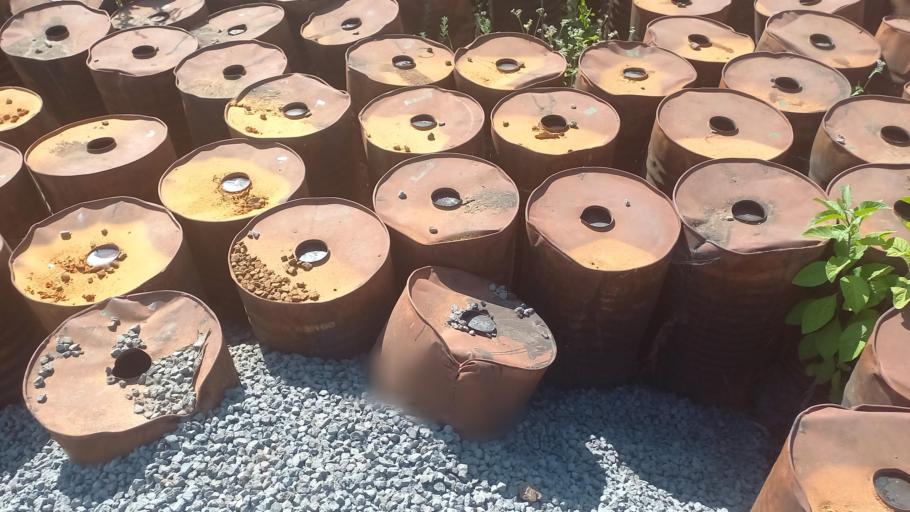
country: ET
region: Southern Nations, Nationalities, and People's Region
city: K'olito
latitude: 7.5397
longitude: 37.8437
